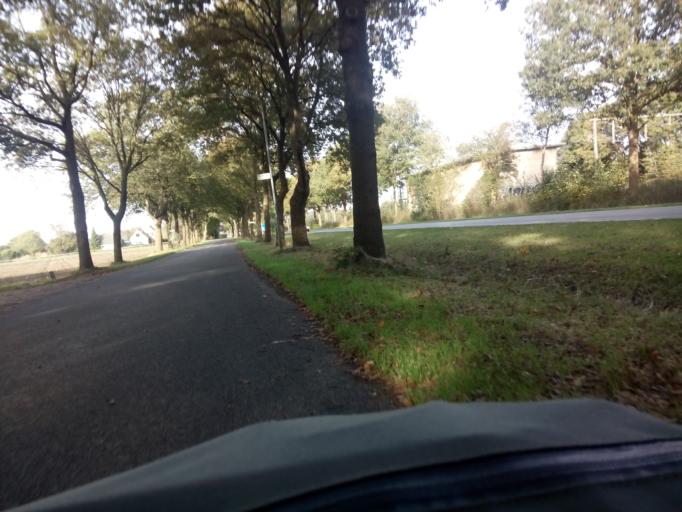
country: NL
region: Drenthe
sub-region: Gemeente Assen
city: Assen
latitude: 52.9130
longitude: 6.5416
